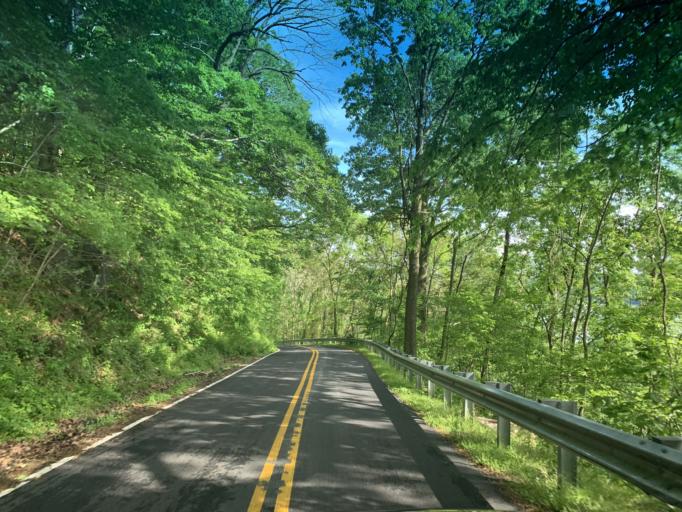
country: US
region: Maryland
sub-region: Cecil County
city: Rising Sun
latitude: 39.6875
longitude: -76.2016
